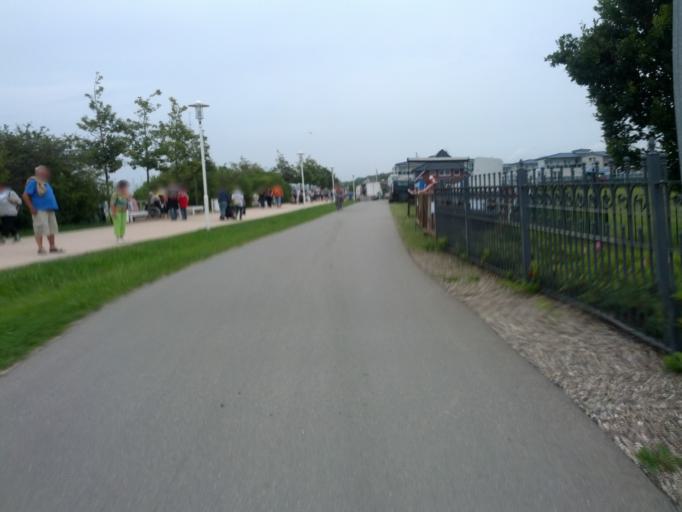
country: DE
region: Mecklenburg-Vorpommern
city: Ostseebad Kuhlungsborn
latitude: 54.1530
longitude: 11.7641
